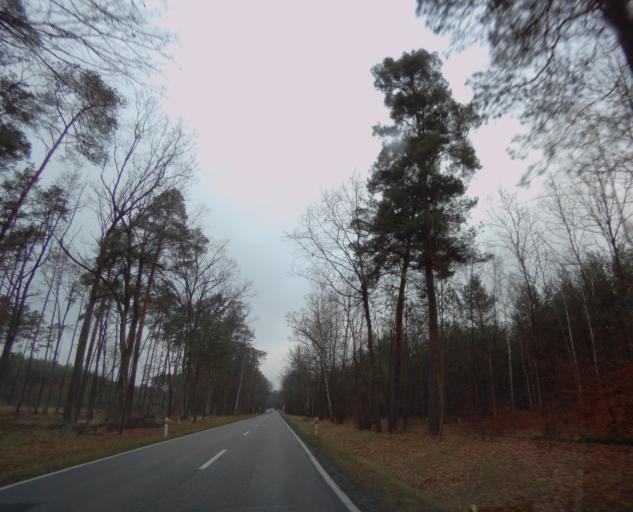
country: PL
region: Subcarpathian Voivodeship
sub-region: Powiat nizanski
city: Krzeszow
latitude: 50.3822
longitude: 22.3093
